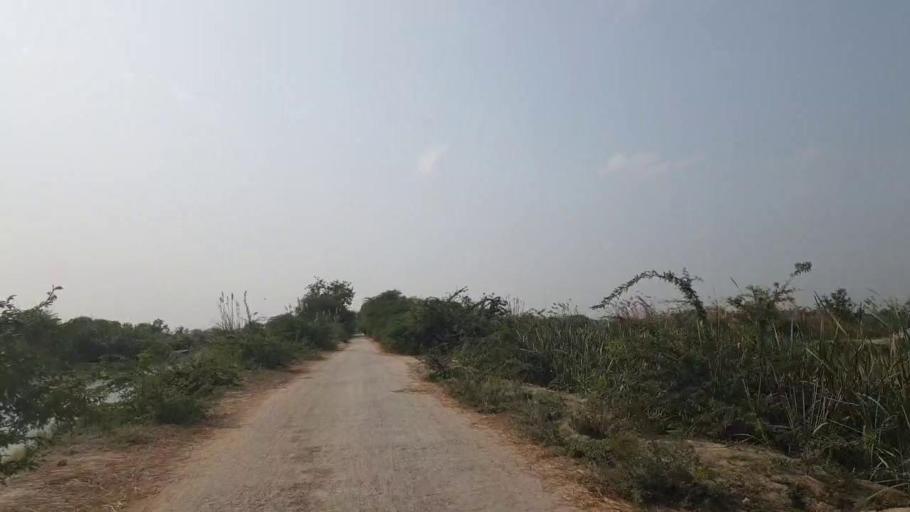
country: PK
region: Sindh
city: Badin
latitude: 24.7619
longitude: 68.7597
